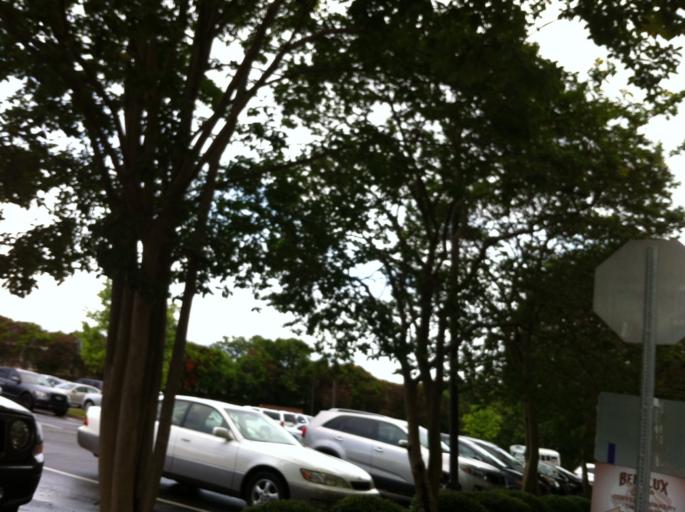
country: US
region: North Carolina
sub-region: Wake County
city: West Raleigh
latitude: 35.7828
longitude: -78.6588
